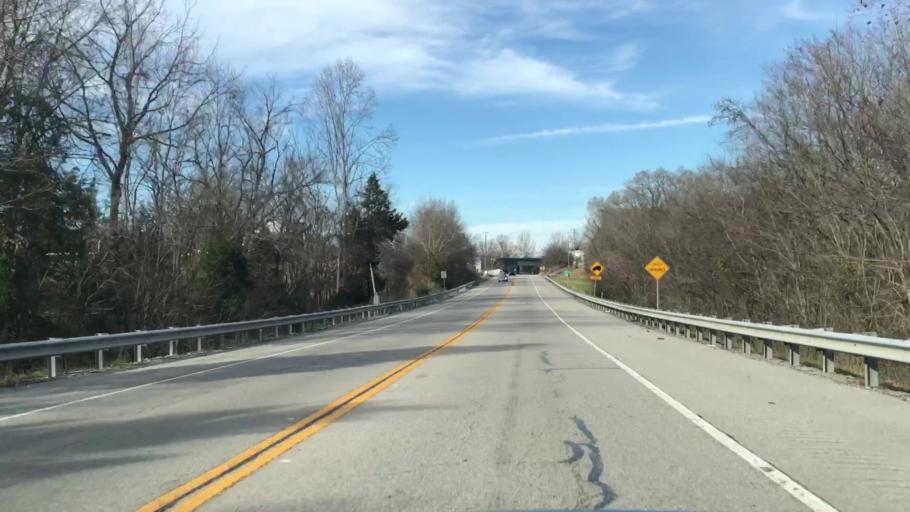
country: US
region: Kentucky
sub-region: Pulaski County
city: Somerset
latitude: 36.9511
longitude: -84.5773
